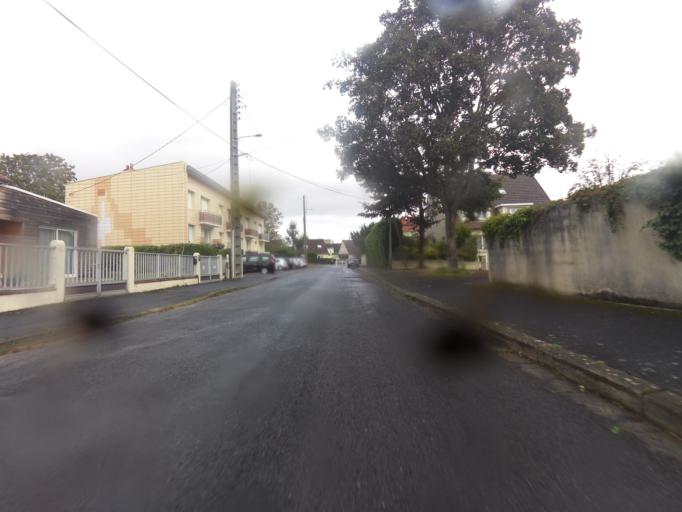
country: FR
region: Lower Normandy
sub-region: Departement du Calvados
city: Caen
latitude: 49.1939
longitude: -0.3543
